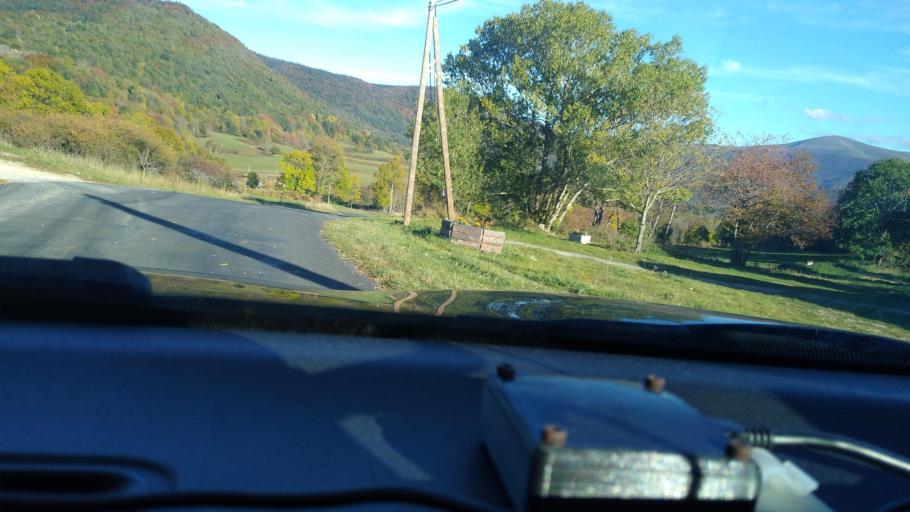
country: FR
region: Languedoc-Roussillon
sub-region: Departement de l'Aude
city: Quillan
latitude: 42.7462
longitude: 2.1668
